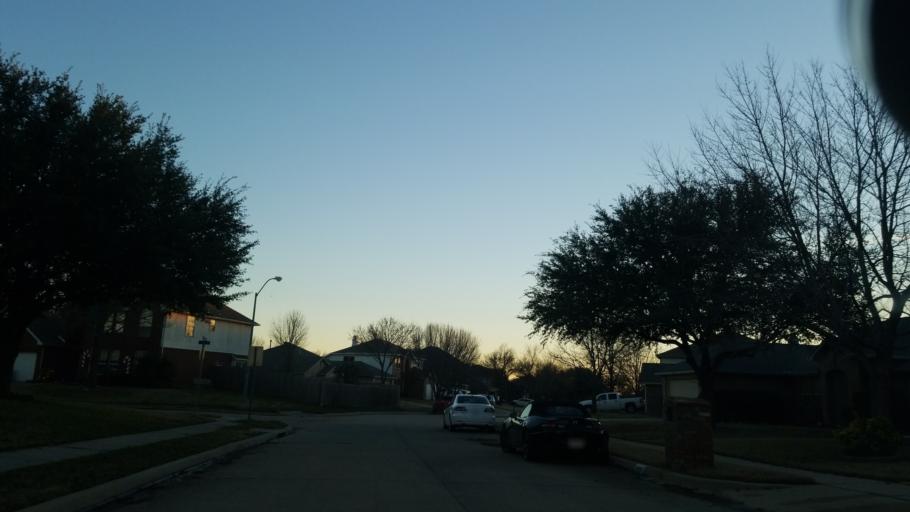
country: US
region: Texas
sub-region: Denton County
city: Corinth
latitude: 33.1384
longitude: -97.0686
